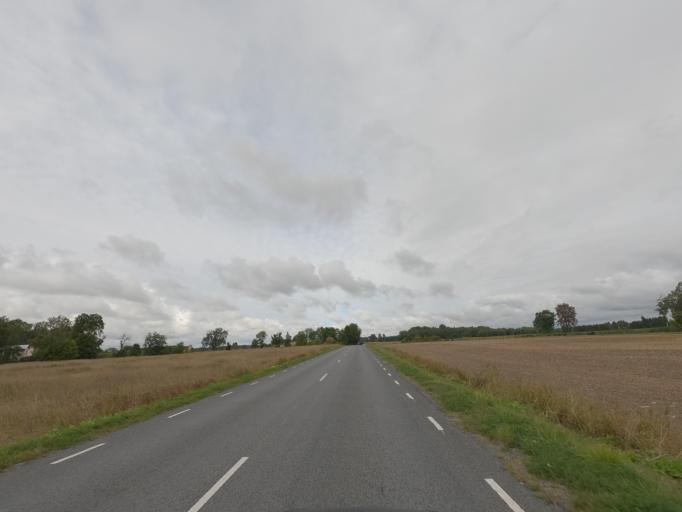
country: EE
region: Raplamaa
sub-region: Maerjamaa vald
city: Marjamaa
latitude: 59.0095
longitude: 24.5718
